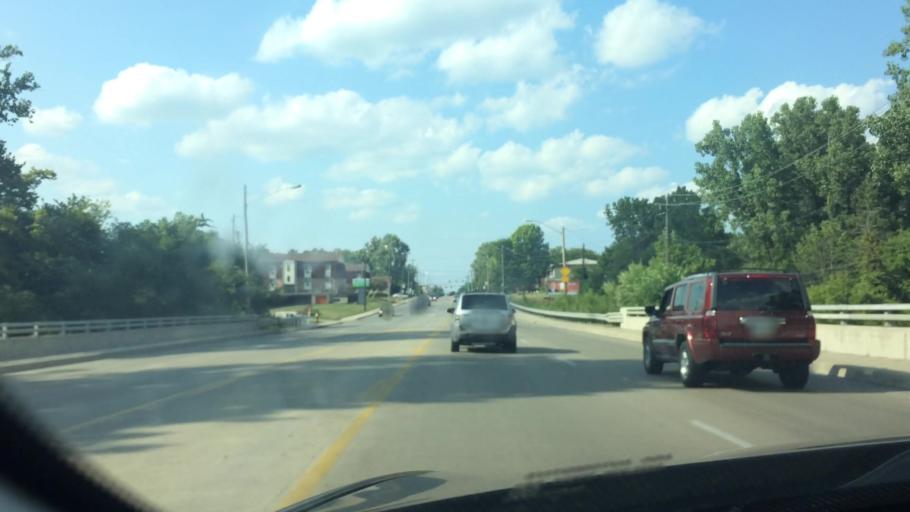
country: US
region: Ohio
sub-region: Lucas County
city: Ottawa Hills
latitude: 41.6195
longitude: -83.6257
